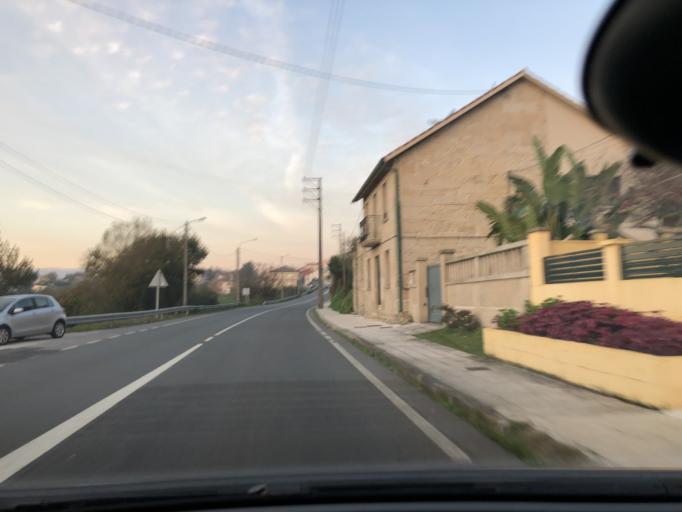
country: ES
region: Galicia
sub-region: Provincia de Pontevedra
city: Marin
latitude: 42.3822
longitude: -8.7155
